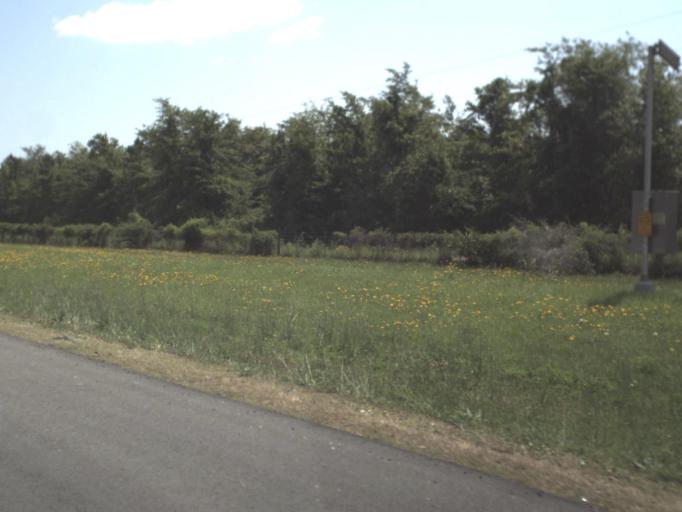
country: US
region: Georgia
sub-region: Camden County
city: Kingsland
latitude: 30.7181
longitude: -81.6678
